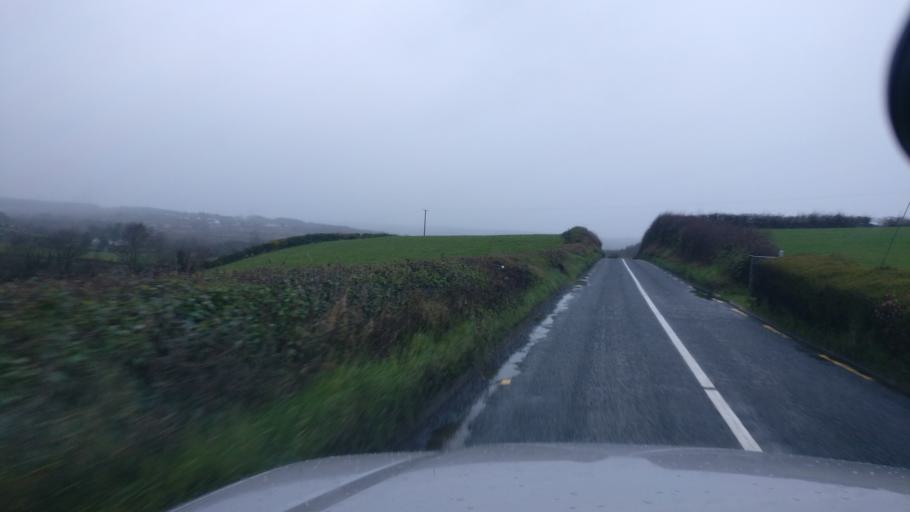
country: IE
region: Connaught
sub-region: County Galway
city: Loughrea
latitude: 53.1181
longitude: -8.4443
